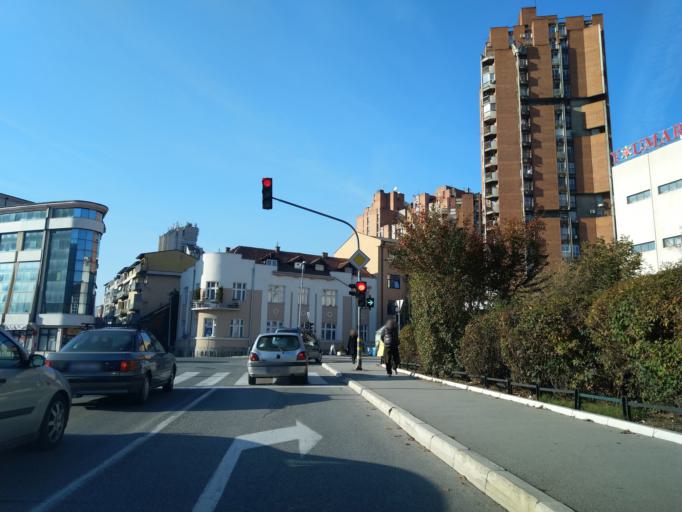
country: RS
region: Central Serbia
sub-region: Zlatiborski Okrug
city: Uzice
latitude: 43.8545
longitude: 19.8427
